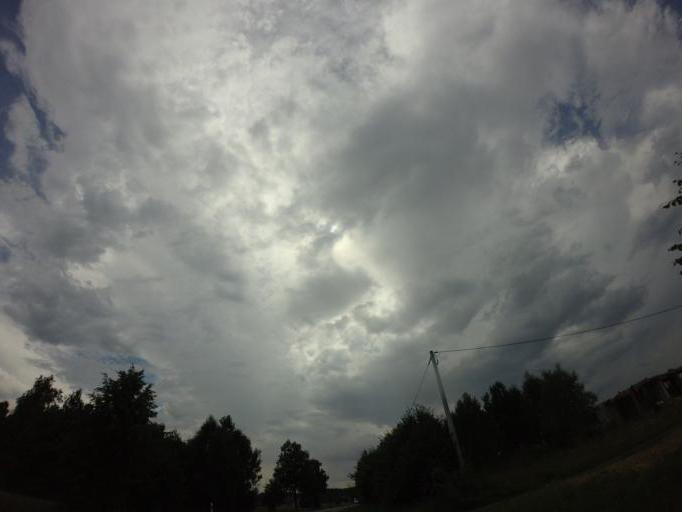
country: PL
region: Swietokrzyskie
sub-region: Powiat staszowski
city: Bogoria
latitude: 50.6165
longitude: 21.2141
